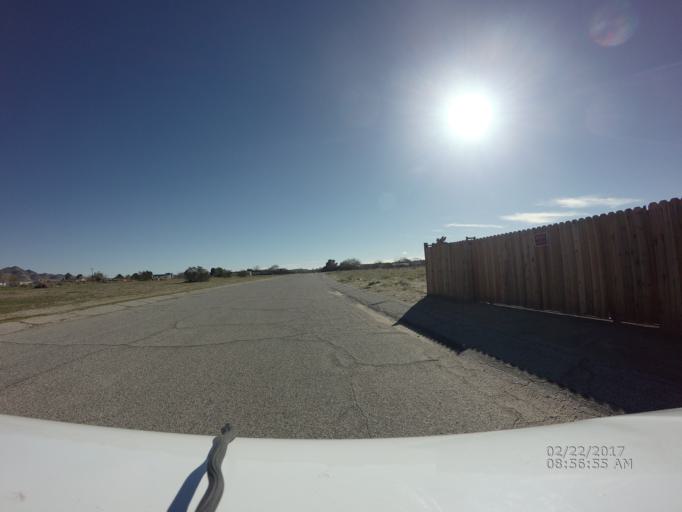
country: US
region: California
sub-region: Los Angeles County
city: Lake Los Angeles
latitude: 34.6276
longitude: -117.8459
